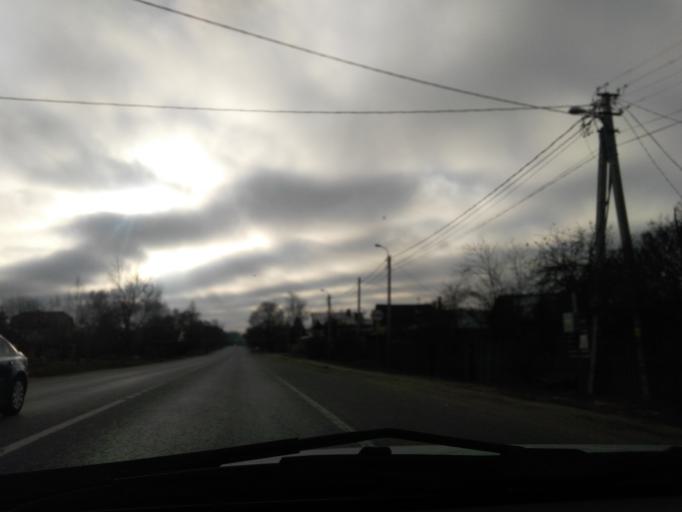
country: RU
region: Moskovskaya
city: Troitsk
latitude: 55.3266
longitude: 37.1635
